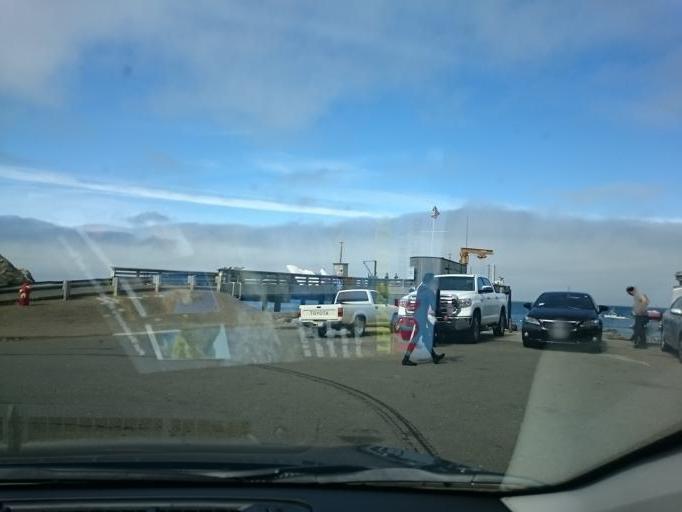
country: US
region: California
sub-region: Sonoma County
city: Sea Ranch
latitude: 38.9148
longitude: -123.7099
